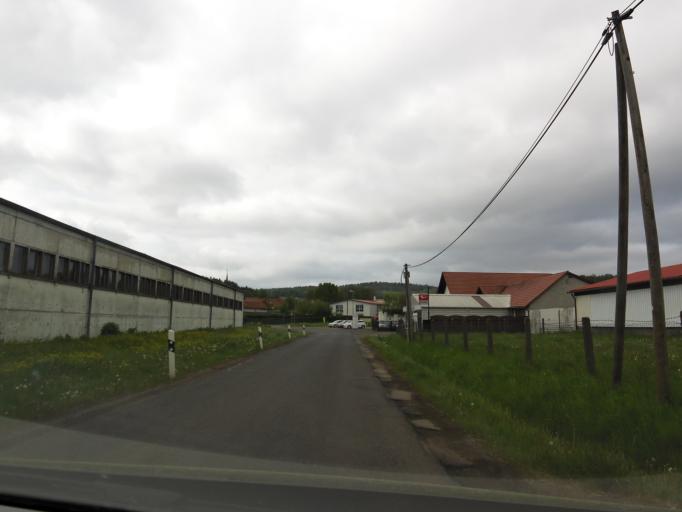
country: DE
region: Thuringia
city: Ernstroda
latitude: 50.8683
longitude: 10.6212
